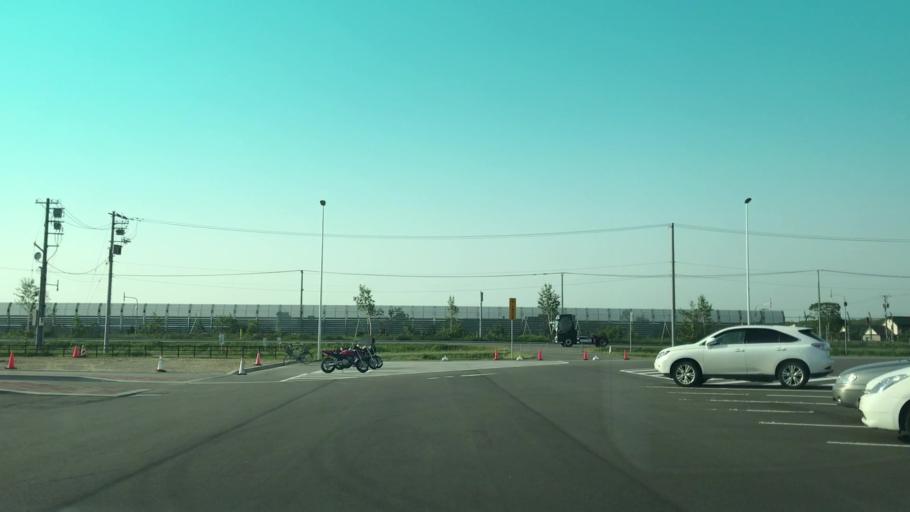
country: JP
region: Hokkaido
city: Tobetsu
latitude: 43.1772
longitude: 141.4486
